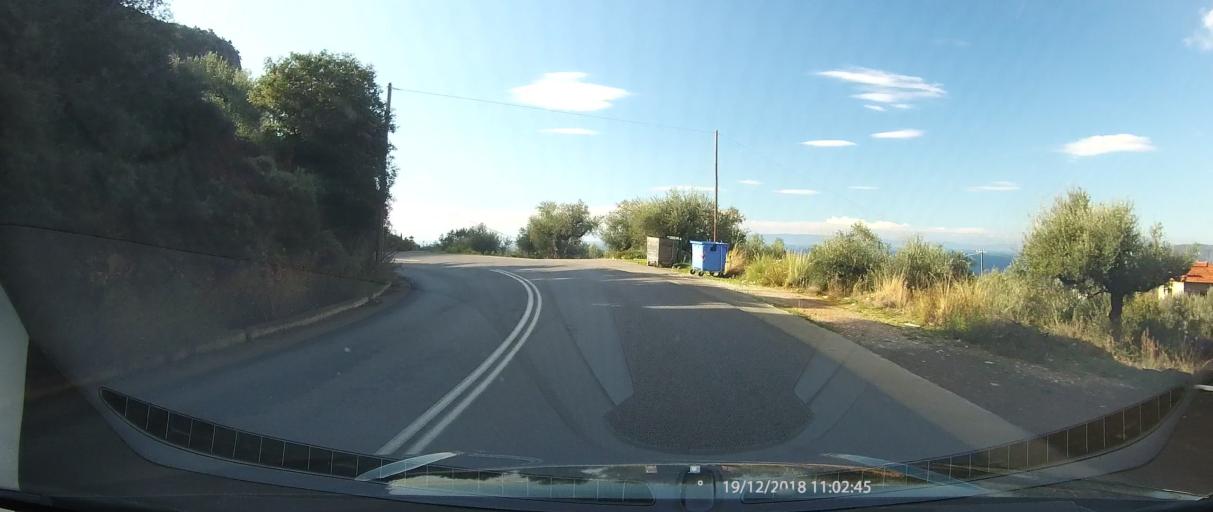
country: GR
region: Peloponnese
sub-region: Nomos Messinias
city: Kardamyli
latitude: 36.8796
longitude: 22.2443
